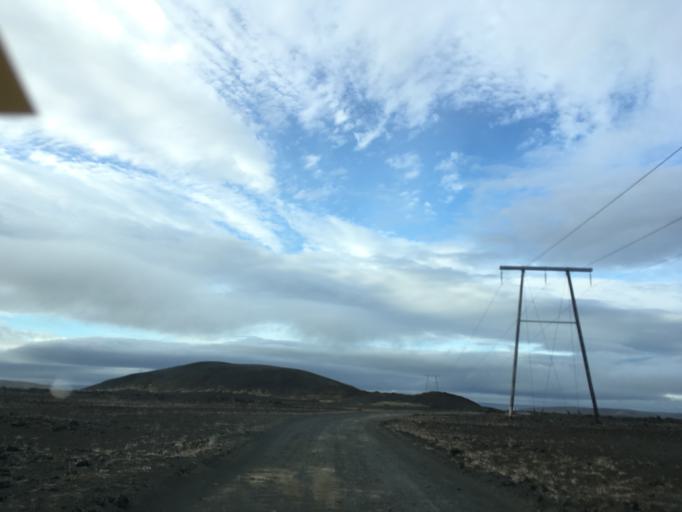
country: IS
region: South
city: Vestmannaeyjar
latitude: 64.1226
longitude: -19.1182
